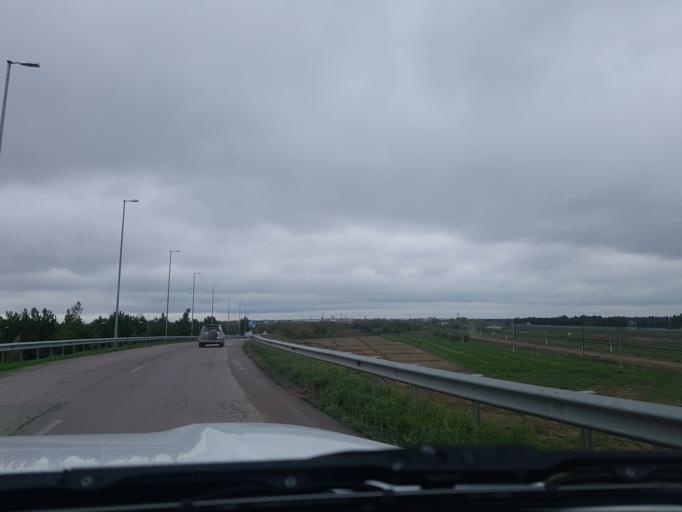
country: TM
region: Mary
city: Mary
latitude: 37.5982
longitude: 61.8881
